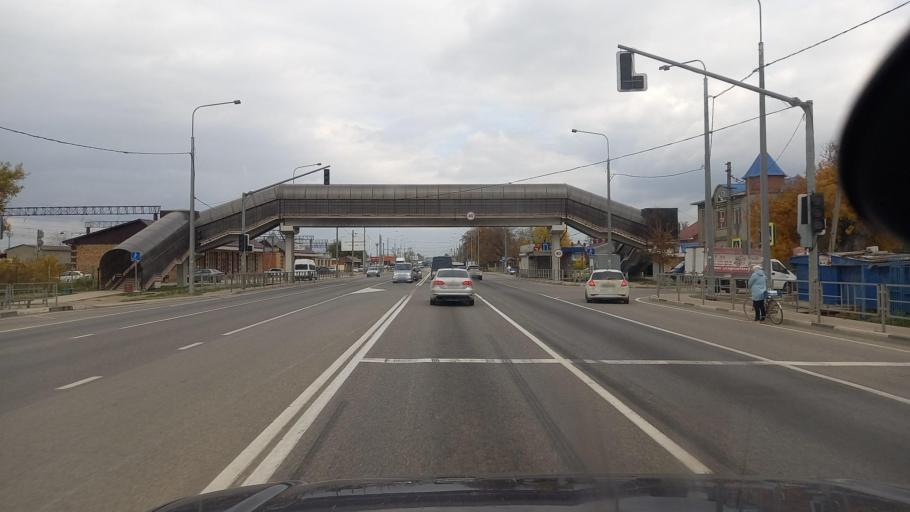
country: RU
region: Adygeya
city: Enem
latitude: 44.9246
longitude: 38.9037
